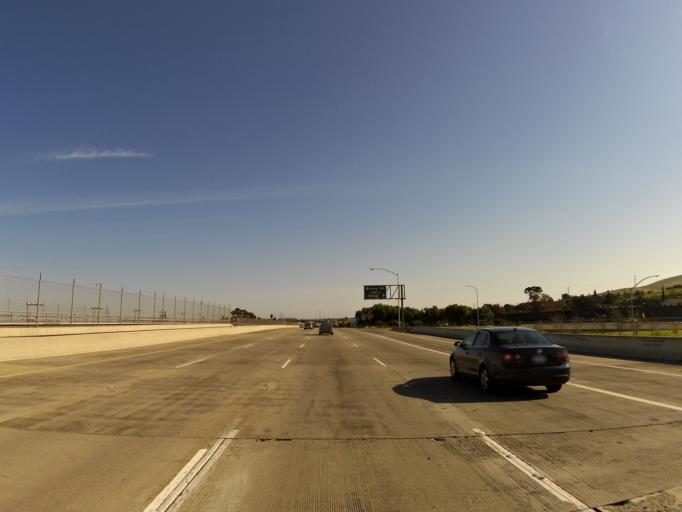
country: US
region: California
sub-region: Contra Costa County
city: Bay Point
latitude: 38.0187
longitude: -121.9426
